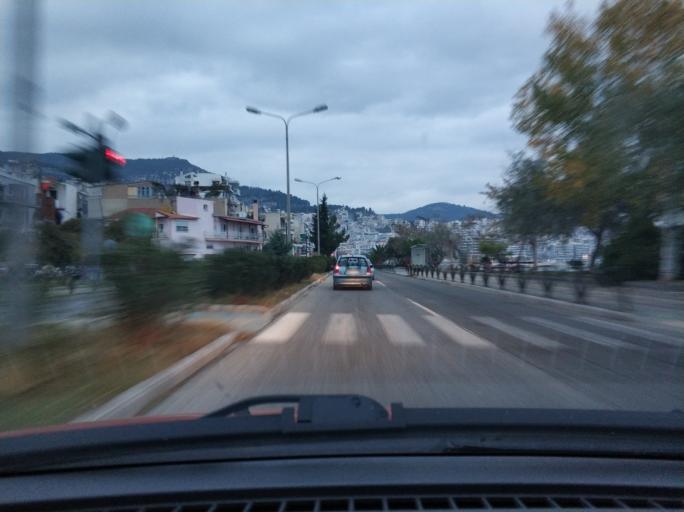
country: GR
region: East Macedonia and Thrace
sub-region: Nomos Kavalas
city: Kavala
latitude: 40.9313
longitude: 24.3921
